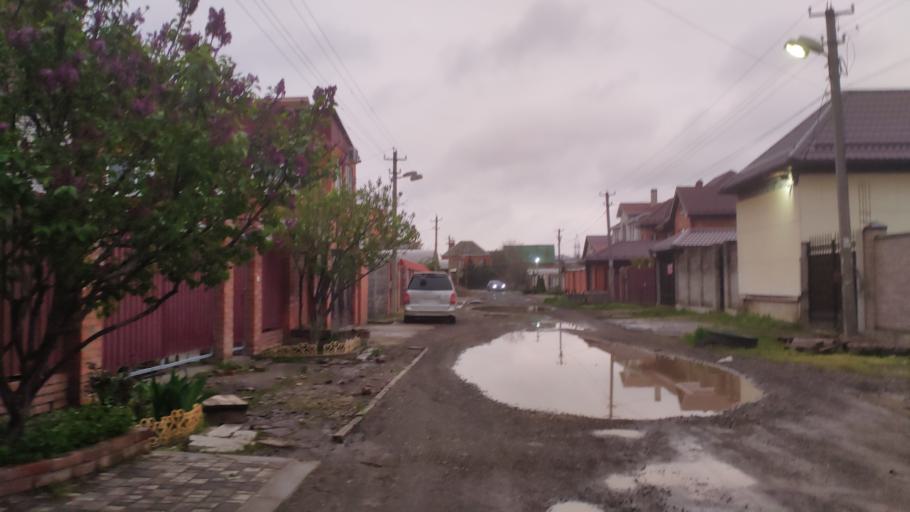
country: RU
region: Krasnodarskiy
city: Krasnodar
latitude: 45.0734
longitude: 39.0106
